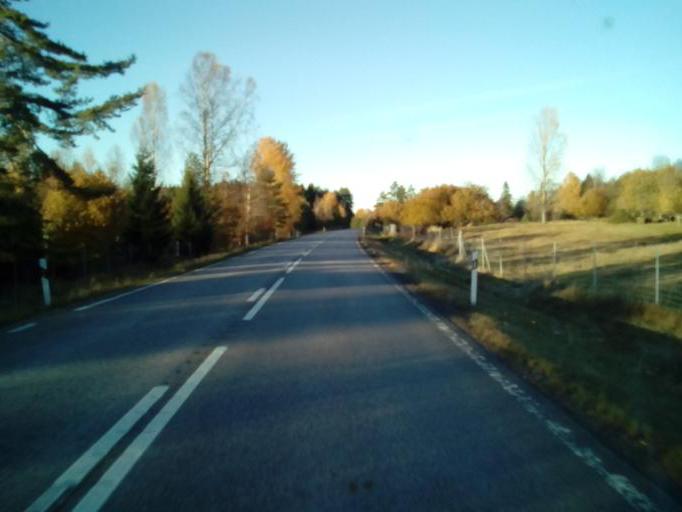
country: SE
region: OErebro
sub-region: Hallsbergs Kommun
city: Palsboda
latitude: 58.9852
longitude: 15.4088
